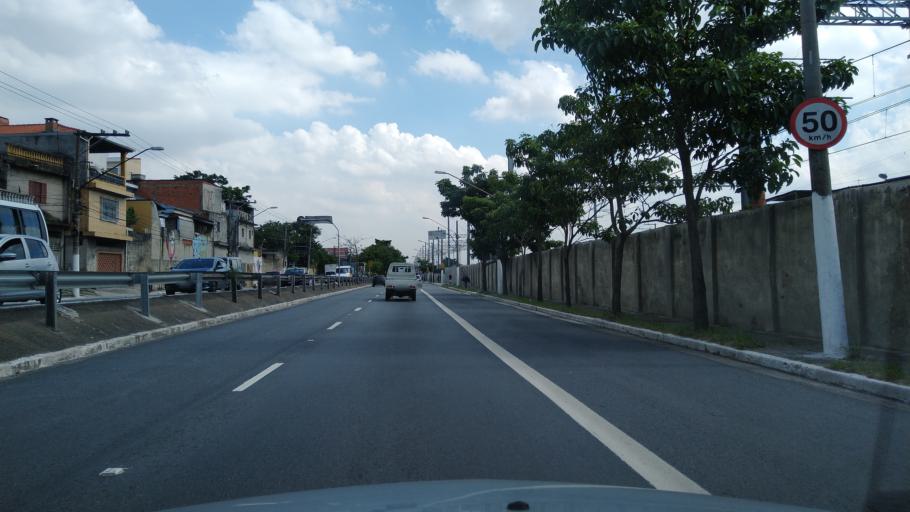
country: BR
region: Sao Paulo
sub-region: Guarulhos
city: Guarulhos
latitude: -23.5006
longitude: -46.5317
